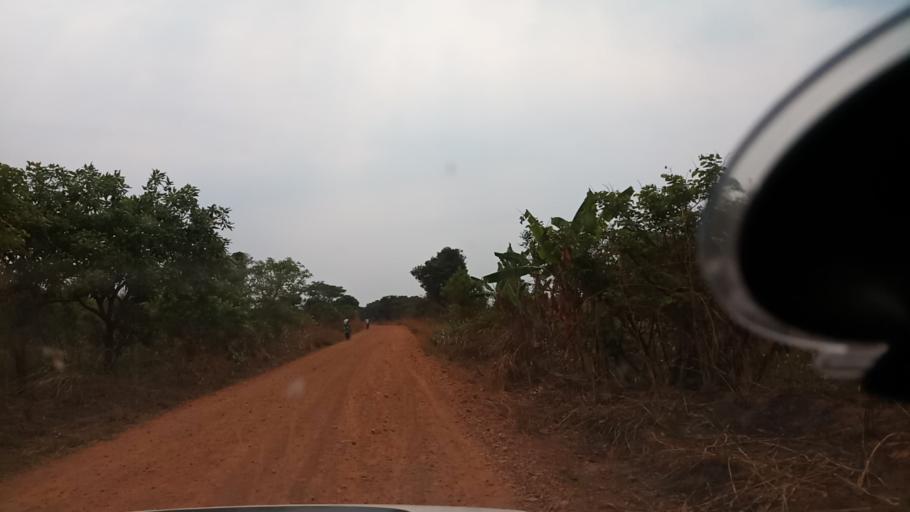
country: ZM
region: Luapula
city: Nchelenge
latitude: -9.0981
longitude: 28.3178
